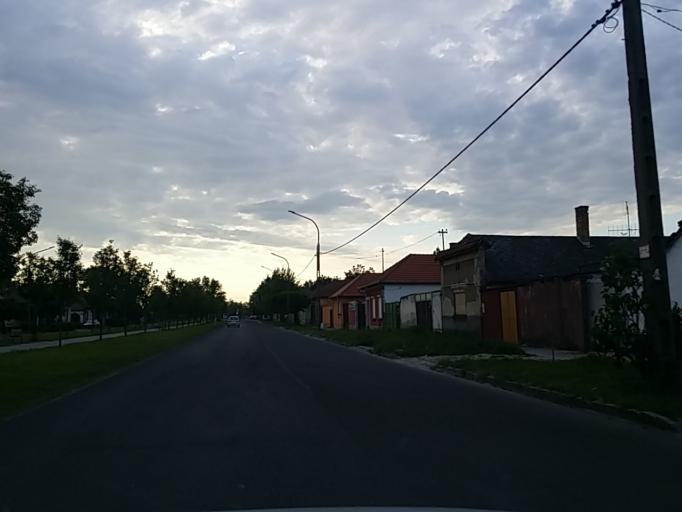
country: HU
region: Bacs-Kiskun
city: Kecskemet
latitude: 46.9008
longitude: 19.7088
